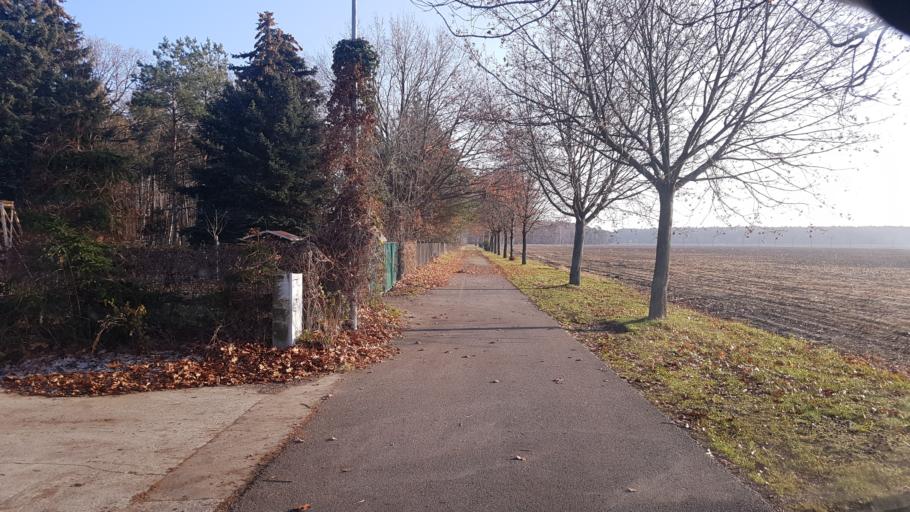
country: DE
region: Brandenburg
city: Tettau
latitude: 51.4360
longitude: 13.7342
